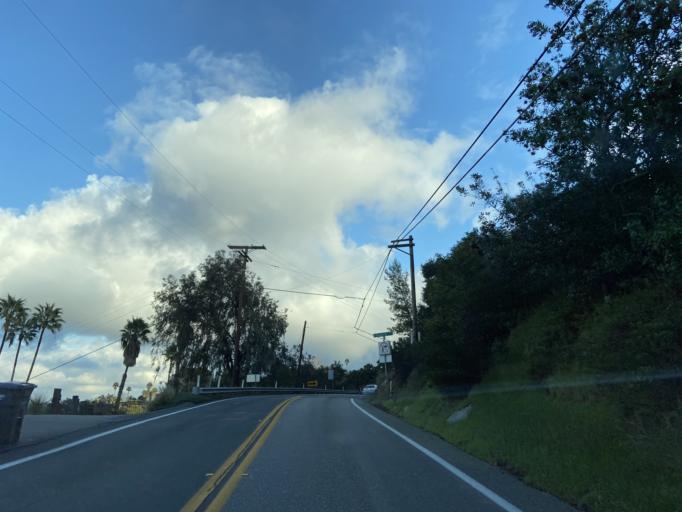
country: US
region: California
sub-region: San Diego County
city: Casa de Oro-Mount Helix
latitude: 32.7762
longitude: -116.9895
